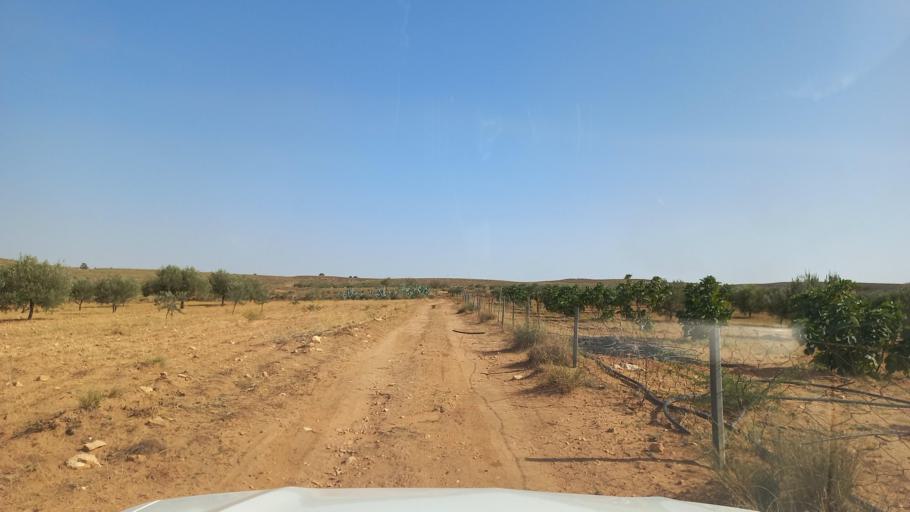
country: TN
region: Al Qasrayn
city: Kasserine
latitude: 35.2055
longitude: 8.9717
